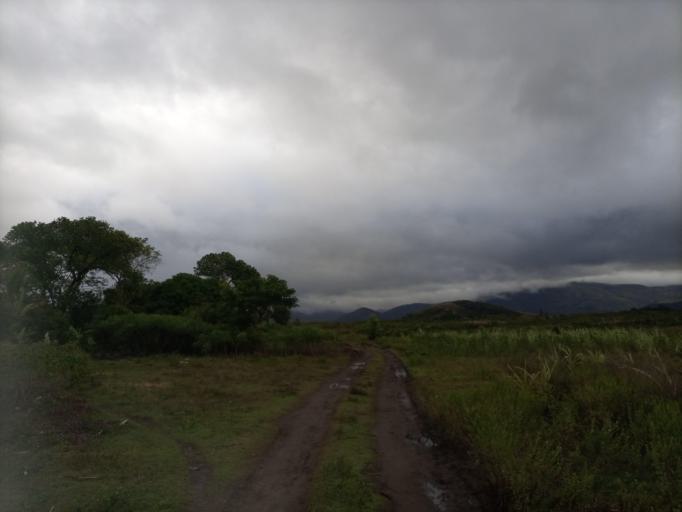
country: MG
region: Anosy
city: Fort Dauphin
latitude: -24.7601
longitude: 47.0690
